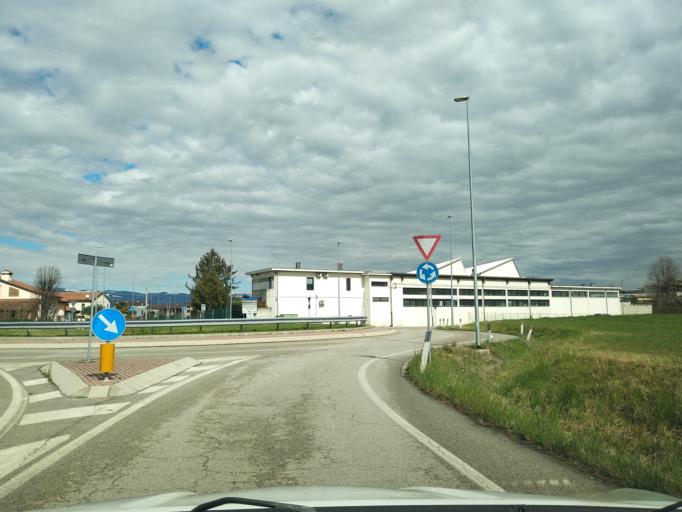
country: IT
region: Veneto
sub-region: Provincia di Vicenza
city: Monticello Conte Otto
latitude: 45.5889
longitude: 11.5793
